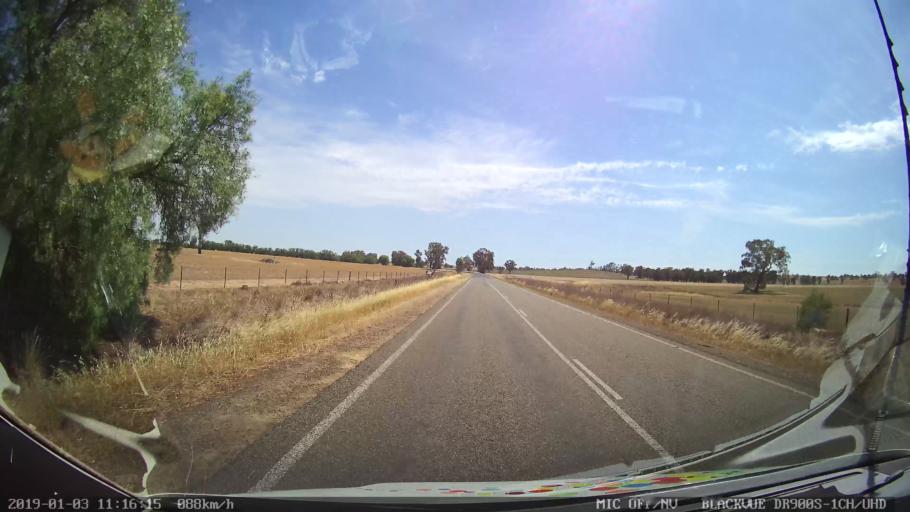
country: AU
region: New South Wales
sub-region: Young
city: Young
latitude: -34.1542
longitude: 148.2694
